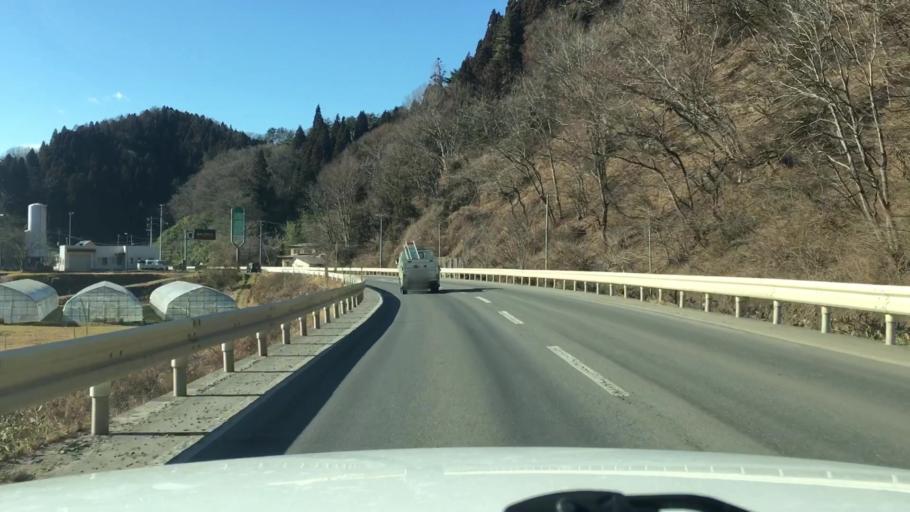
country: JP
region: Iwate
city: Miyako
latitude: 39.6326
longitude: 141.8829
